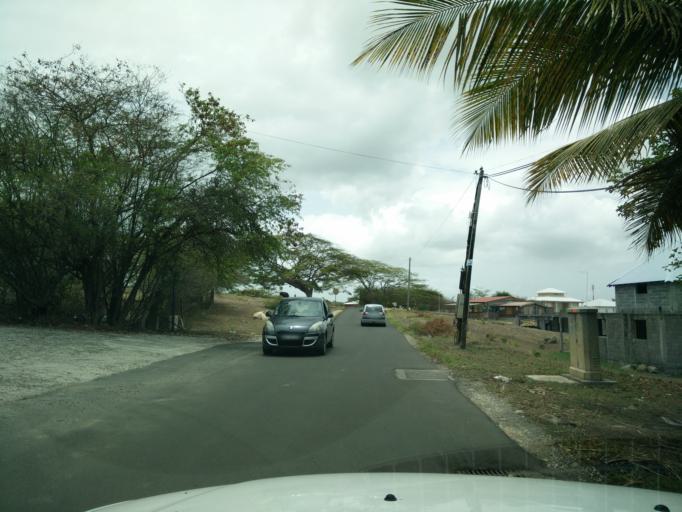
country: GP
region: Guadeloupe
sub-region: Guadeloupe
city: Sainte-Anne
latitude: 16.2470
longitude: -61.3567
